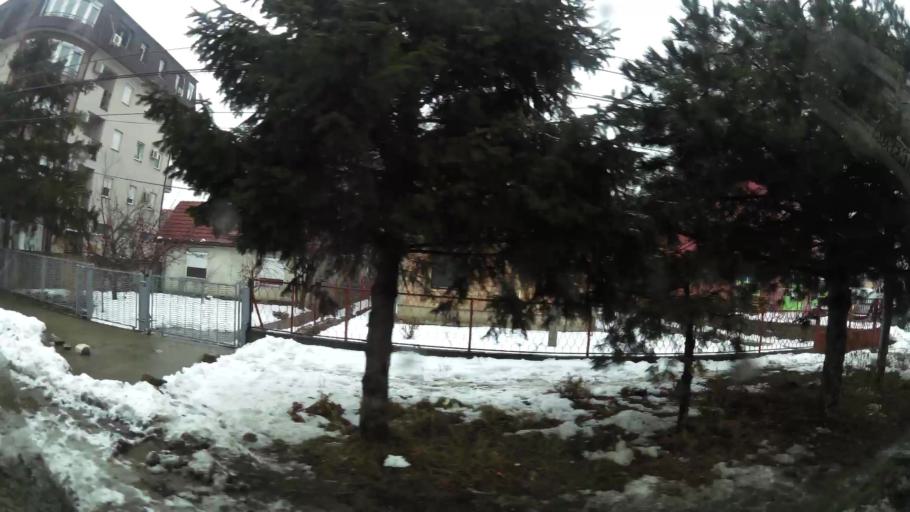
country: RS
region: Central Serbia
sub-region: Belgrade
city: Zemun
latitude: 44.8530
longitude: 20.3632
